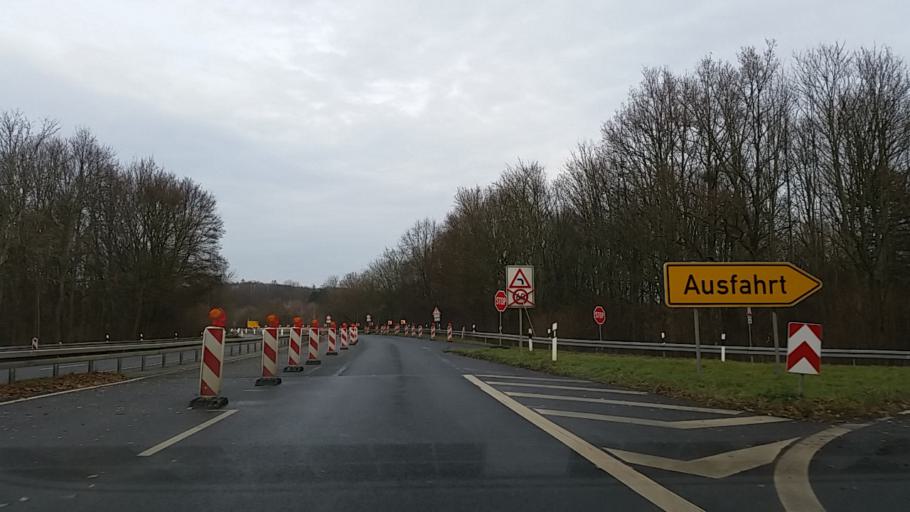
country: DE
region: Lower Saxony
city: Alt Wallmoden
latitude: 52.0415
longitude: 10.3571
